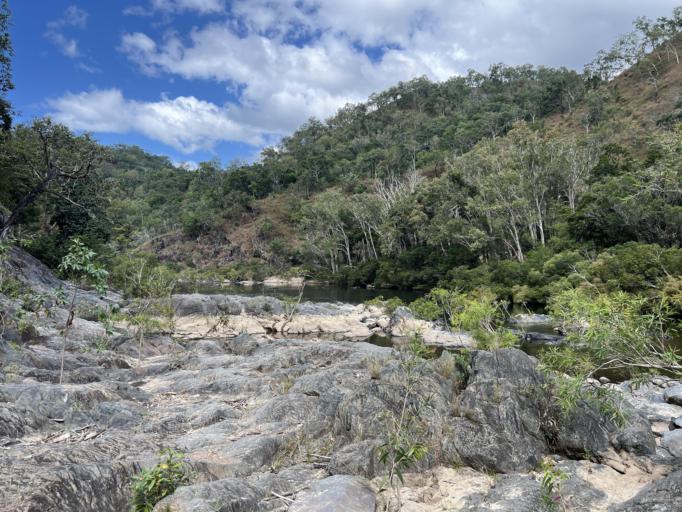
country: AU
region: Queensland
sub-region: Cook
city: Cooktown
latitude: -15.9623
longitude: 145.3143
